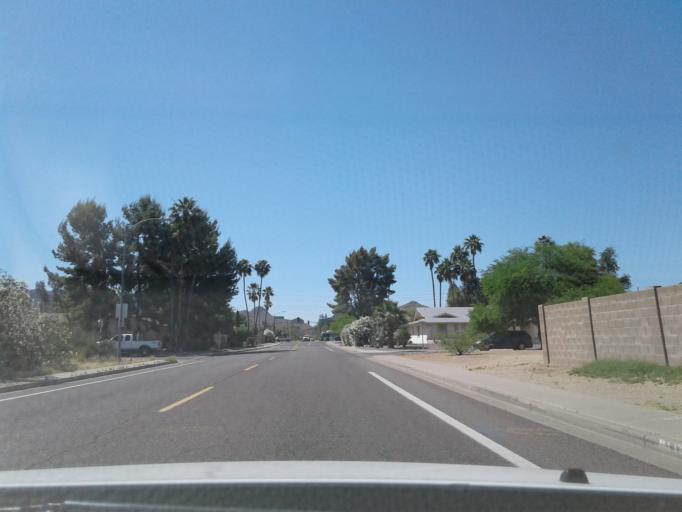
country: US
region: Arizona
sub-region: Maricopa County
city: Paradise Valley
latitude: 33.5844
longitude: -112.0045
